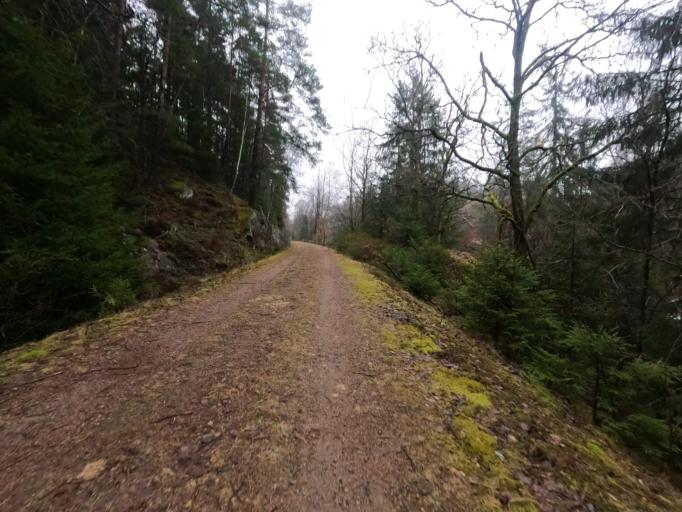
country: SE
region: Halland
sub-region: Hylte Kommun
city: Hyltebruk
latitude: 56.8004
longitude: 13.2424
